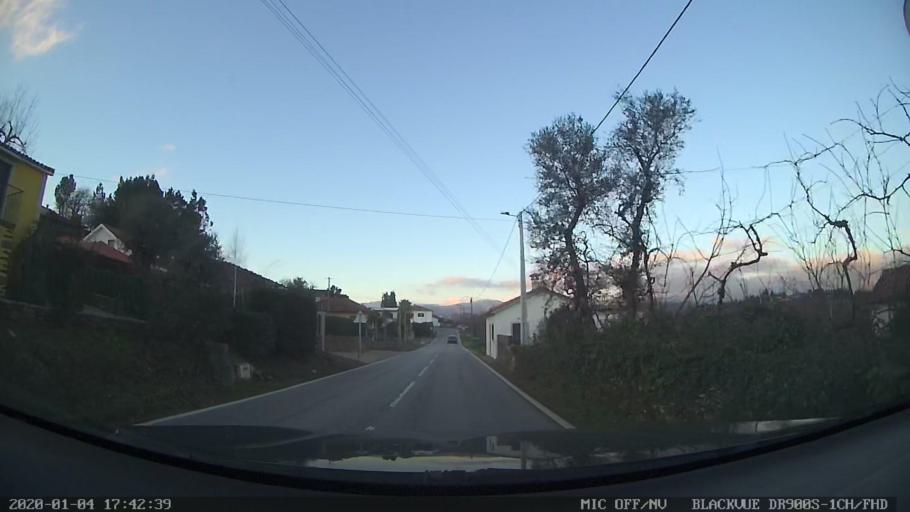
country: PT
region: Braga
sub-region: Cabeceiras de Basto
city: Cabeceiras de Basto
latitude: 41.4714
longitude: -7.9501
